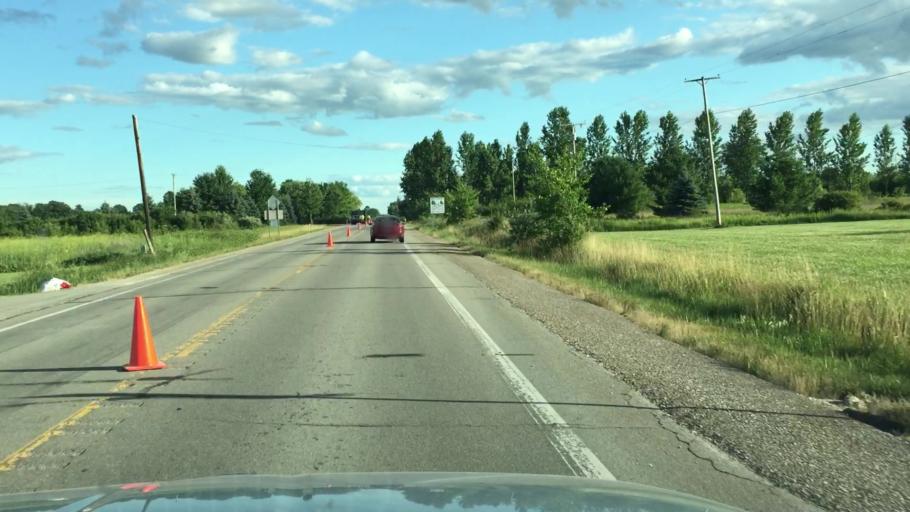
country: US
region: Michigan
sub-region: Saint Clair County
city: Yale
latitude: 43.1007
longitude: -82.7668
